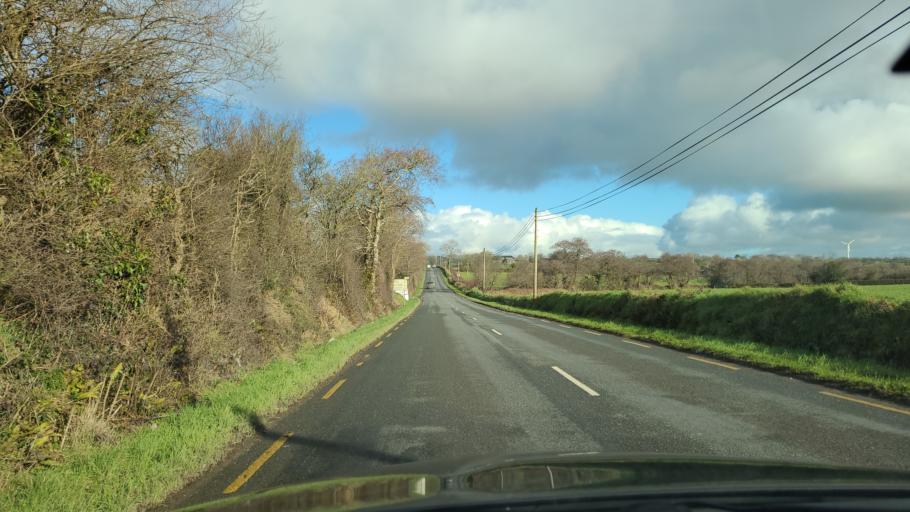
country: IE
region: Munster
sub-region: County Cork
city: Bandon
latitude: 51.7624
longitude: -8.7270
